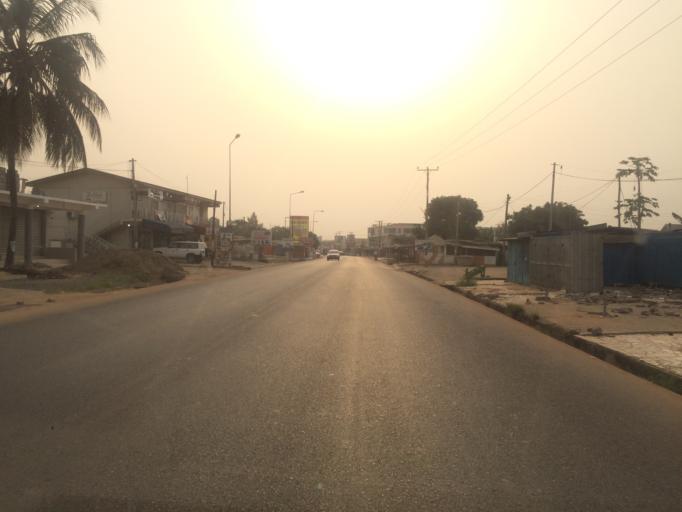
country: GH
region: Greater Accra
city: Nungua
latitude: 5.6268
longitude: -0.0849
